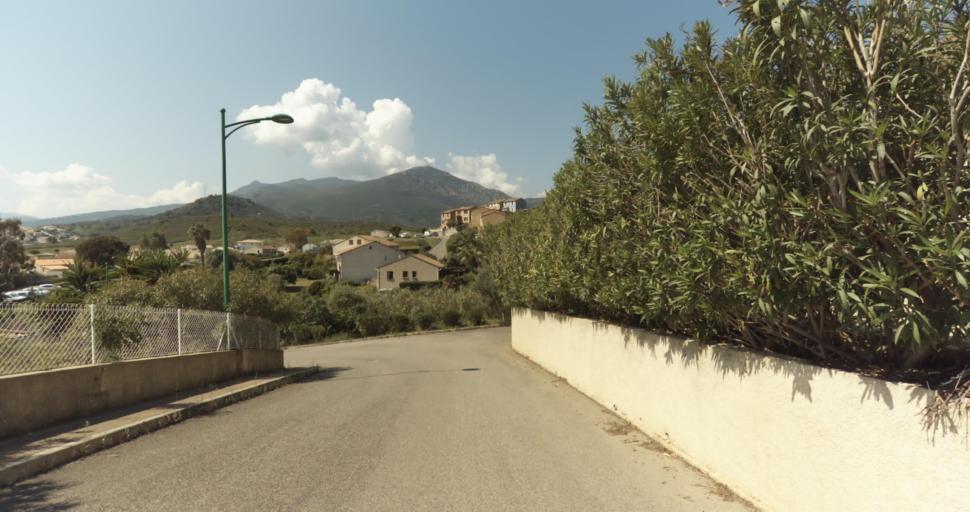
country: FR
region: Corsica
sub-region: Departement de la Haute-Corse
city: Biguglia
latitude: 42.6164
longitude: 9.4305
